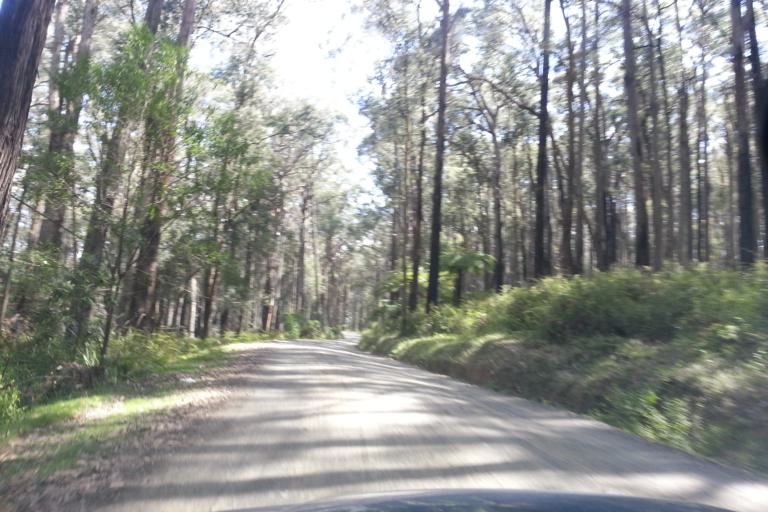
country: AU
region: Victoria
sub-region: Cardinia
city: Gembrook
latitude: -37.9397
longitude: 145.5860
